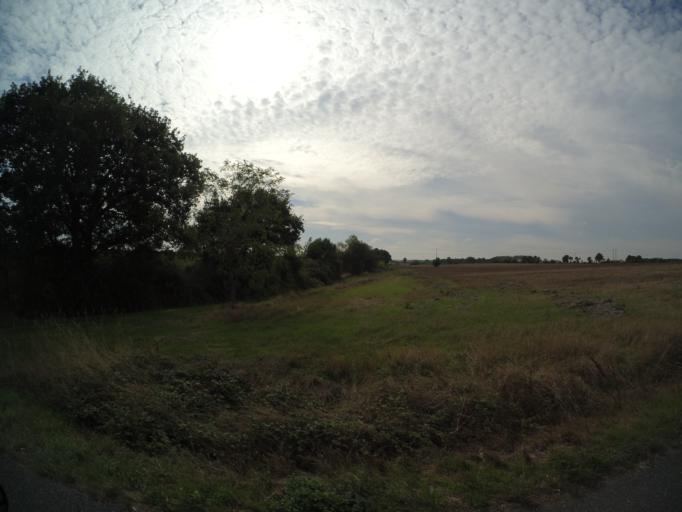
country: FR
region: Pays de la Loire
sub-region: Departement de Maine-et-Loire
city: Martigne-Briand
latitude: 47.2084
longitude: -0.4806
